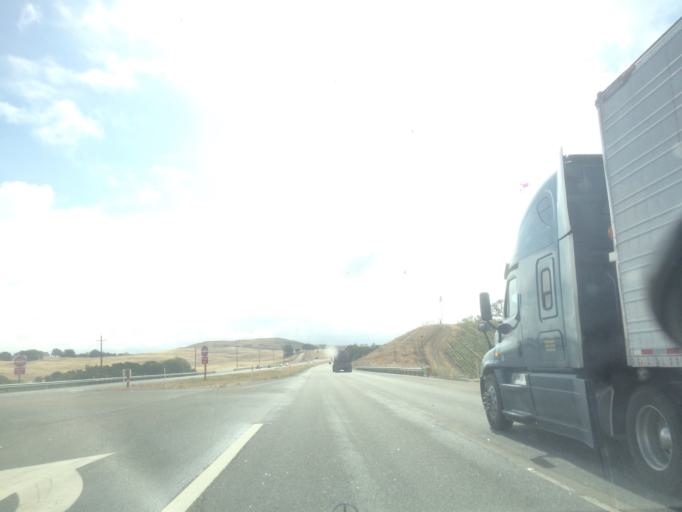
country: US
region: California
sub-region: San Luis Obispo County
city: Paso Robles
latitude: 35.6593
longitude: -120.5520
